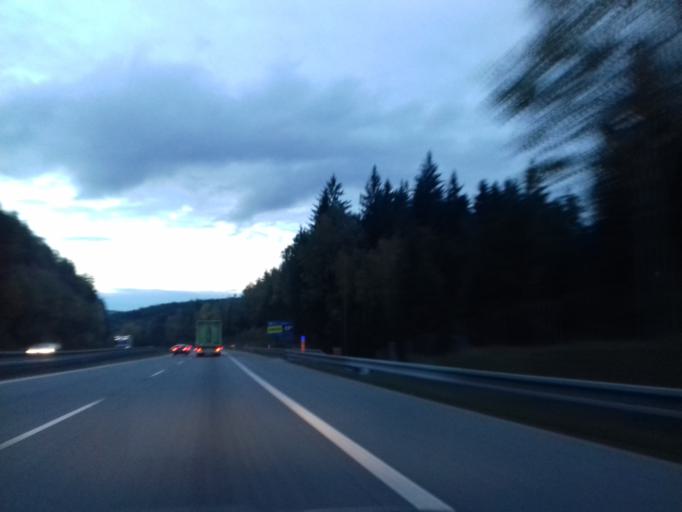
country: CZ
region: Central Bohemia
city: Vlasim
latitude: 49.7644
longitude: 14.9514
